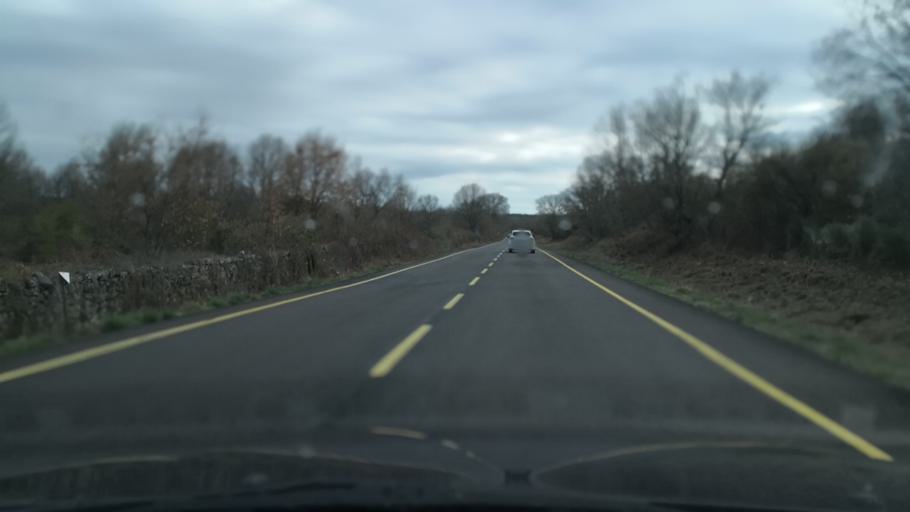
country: ES
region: Castille and Leon
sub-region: Provincia de Salamanca
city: Penaparda
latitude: 40.2787
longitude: -6.6777
